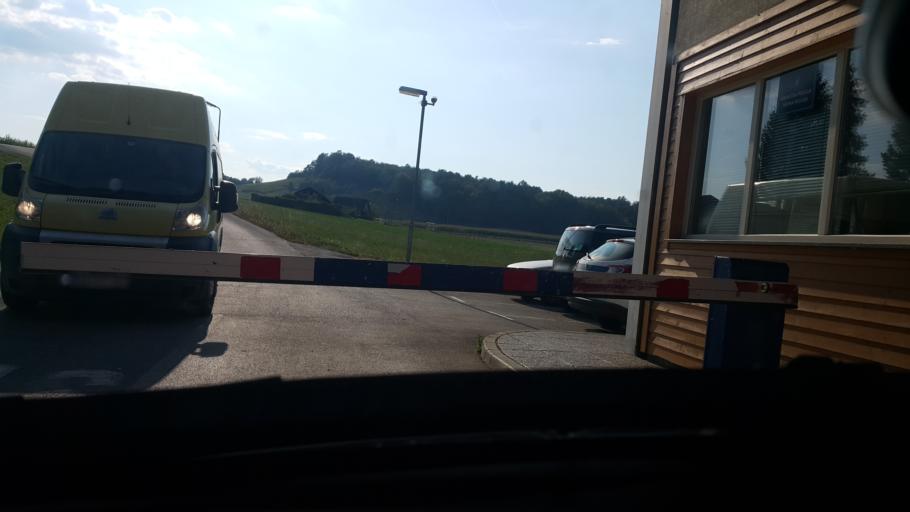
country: SI
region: Podcetrtek
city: Podcetrtek
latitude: 46.0998
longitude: 15.6148
